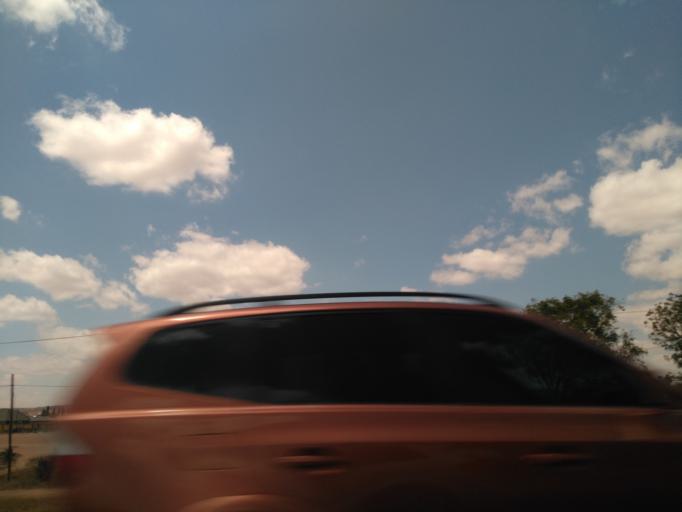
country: TZ
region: Dodoma
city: Kisasa
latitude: -6.1672
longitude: 35.7815
